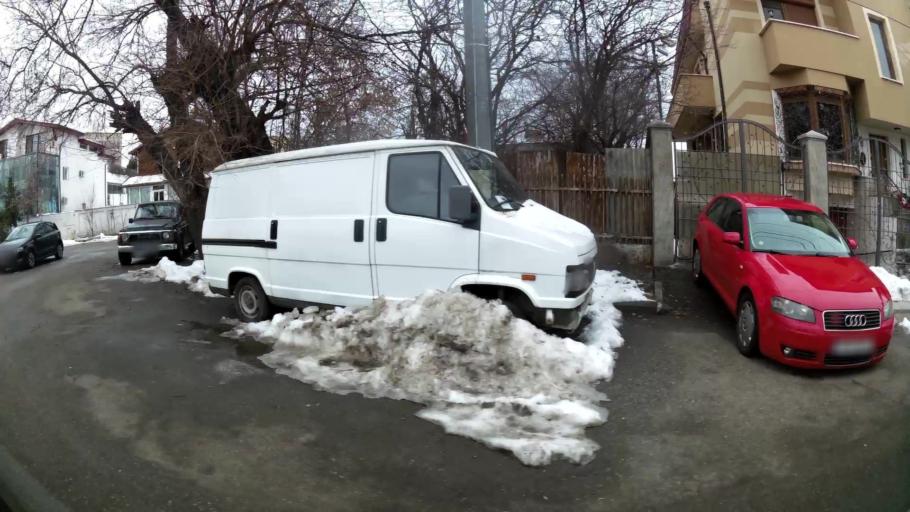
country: RO
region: Bucuresti
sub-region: Municipiul Bucuresti
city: Bucuresti
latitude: 44.4233
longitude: 26.0555
